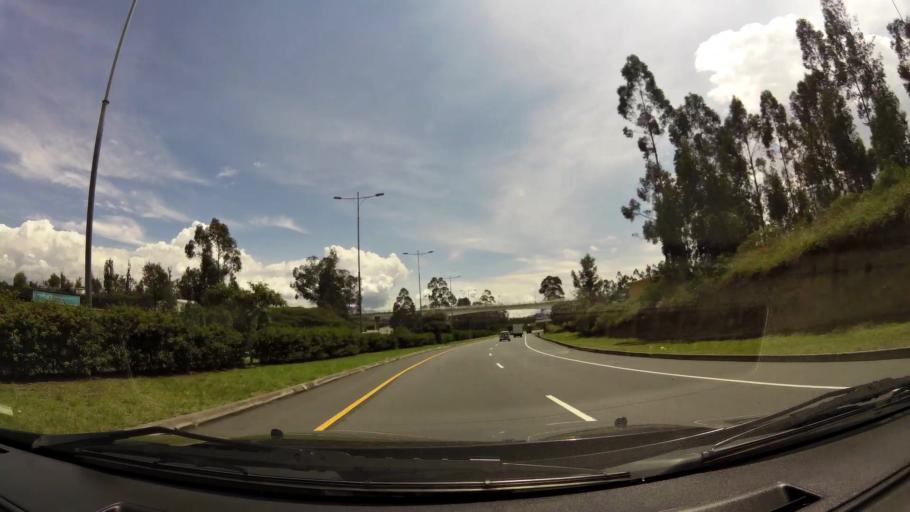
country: EC
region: Pichincha
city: Sangolqui
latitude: -0.1807
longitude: -78.3406
